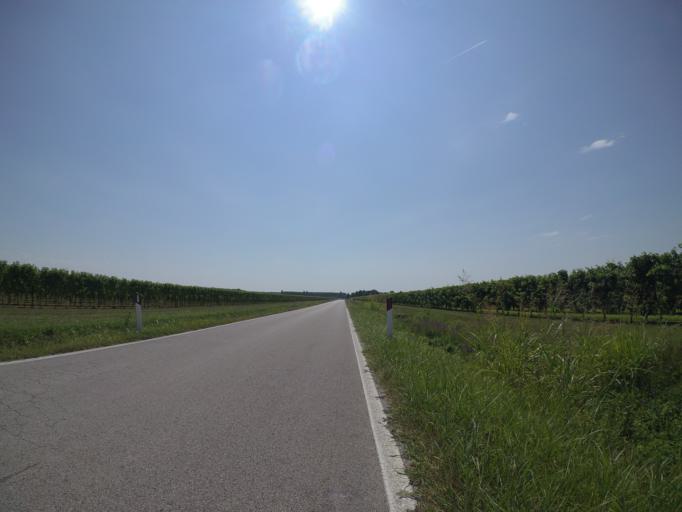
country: IT
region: Friuli Venezia Giulia
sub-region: Provincia di Udine
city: Codroipo
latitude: 45.9425
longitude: 13.0111
